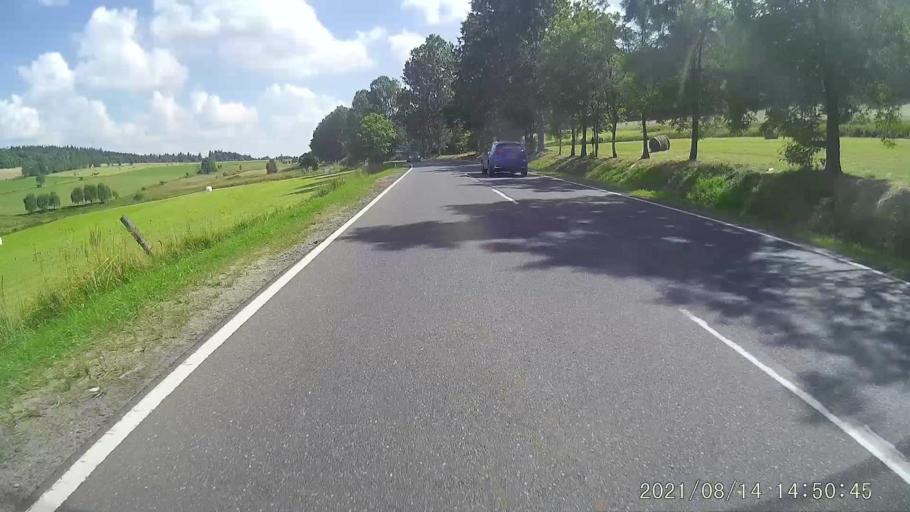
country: PL
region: Lower Silesian Voivodeship
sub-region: Powiat walbrzyski
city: Gluszyca Gorna
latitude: 50.6553
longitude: 16.3753
